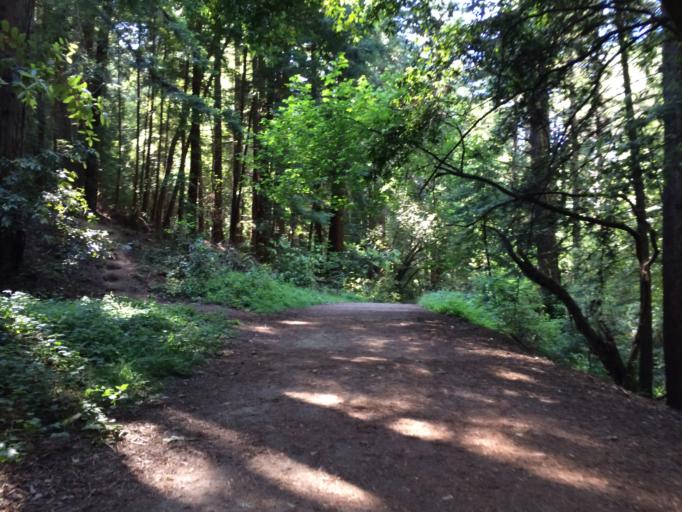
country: US
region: California
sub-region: Santa Cruz County
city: Mount Hermon
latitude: 37.0313
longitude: -122.0603
